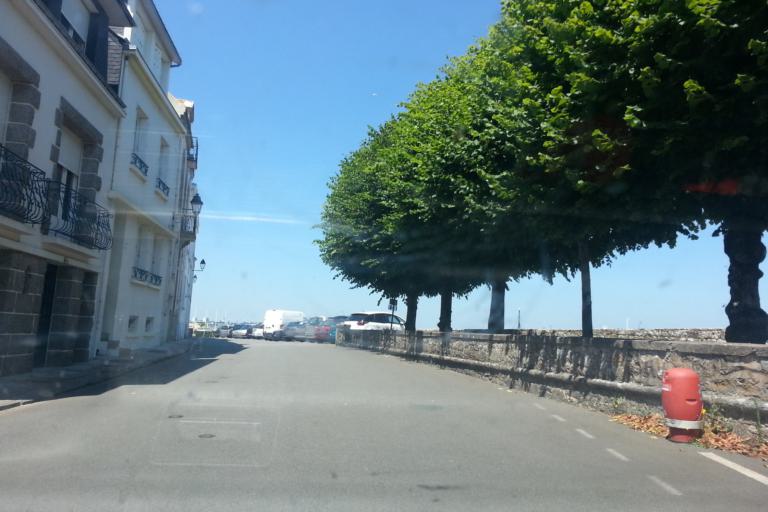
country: FR
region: Brittany
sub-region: Departement du Morbihan
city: Port-Louis
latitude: 47.7108
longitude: -3.3546
